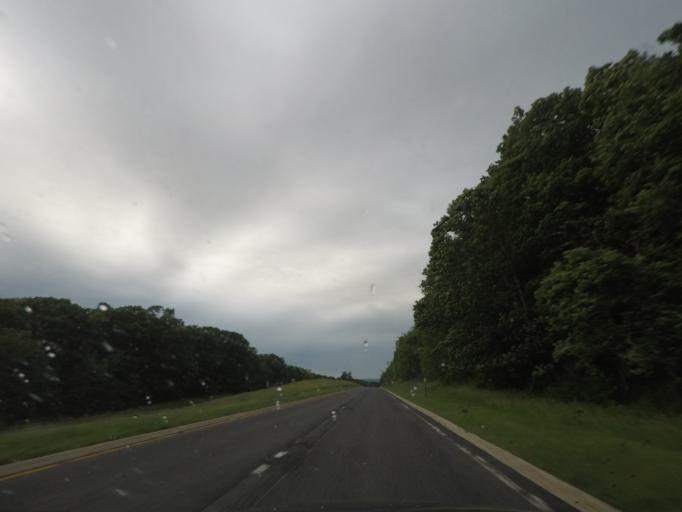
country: US
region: New York
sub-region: Columbia County
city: Chatham
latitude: 42.3188
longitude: -73.5764
